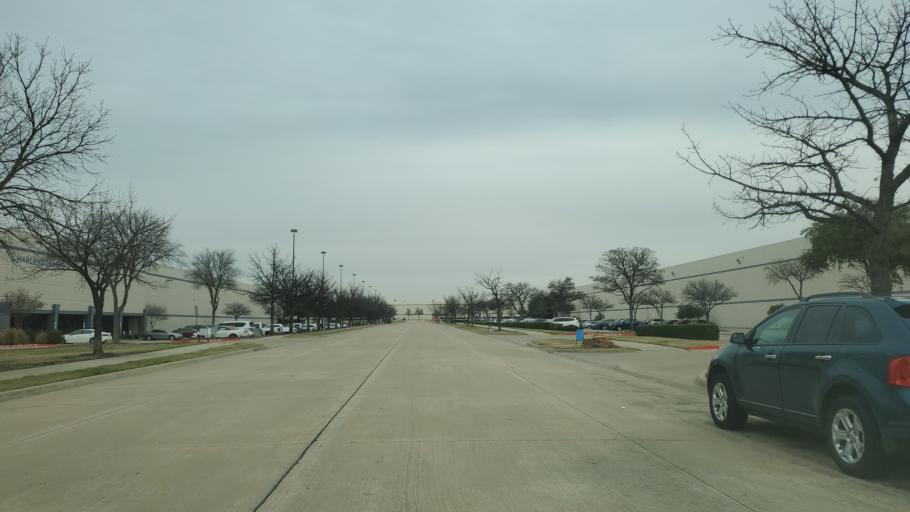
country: US
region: Texas
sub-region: Dallas County
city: Coppell
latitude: 32.9812
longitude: -97.0275
